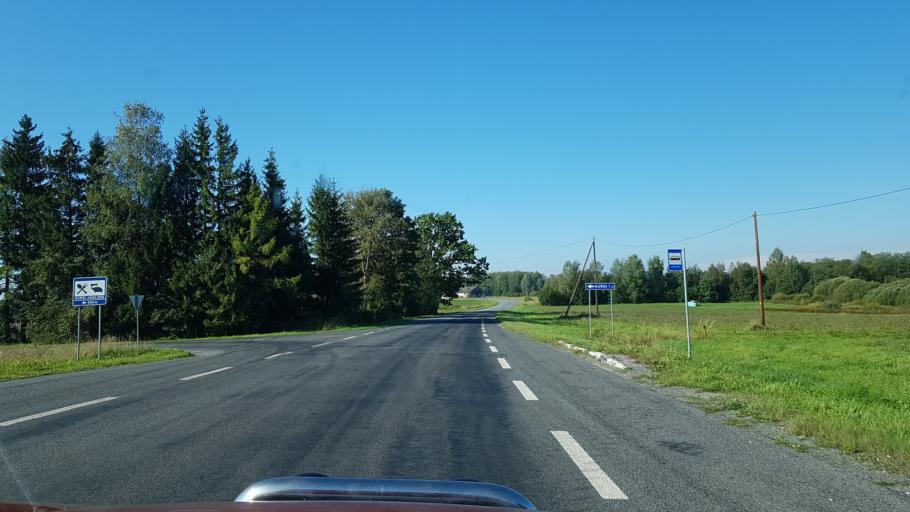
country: EE
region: Jogevamaa
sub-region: Jogeva linn
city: Jogeva
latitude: 58.6009
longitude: 26.3217
